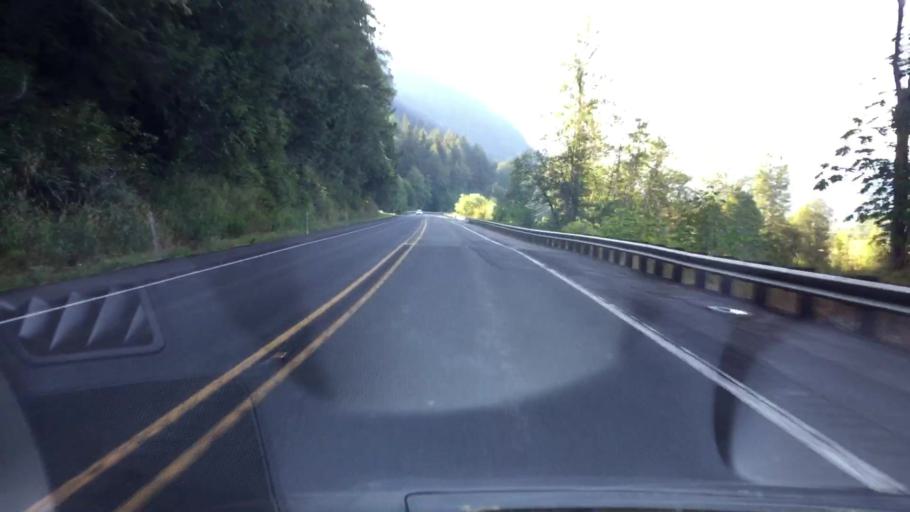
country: US
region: Washington
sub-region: Lewis County
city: Morton
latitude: 46.5253
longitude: -122.2295
